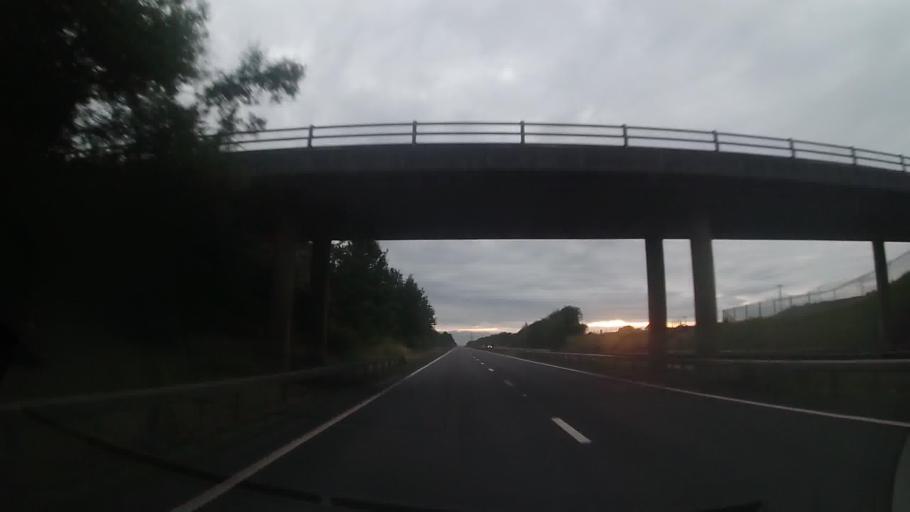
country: GB
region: England
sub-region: Shropshire
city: Withington
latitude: 52.7023
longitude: -2.6606
